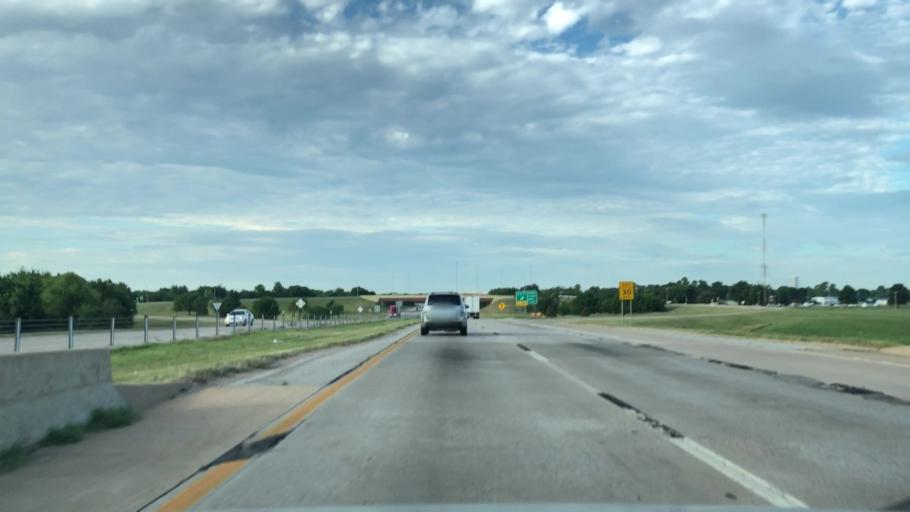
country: US
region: Oklahoma
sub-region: Tulsa County
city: Turley
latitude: 36.2102
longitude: -95.9458
